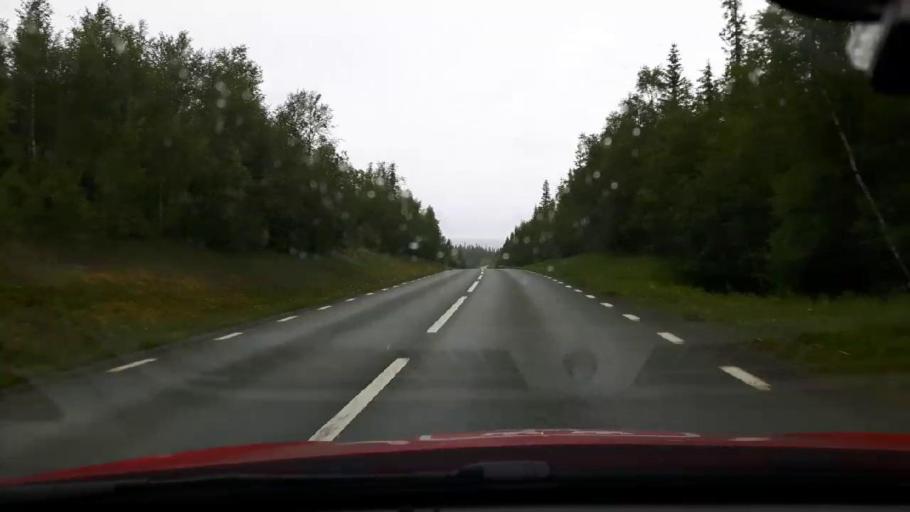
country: NO
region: Nord-Trondelag
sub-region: Meraker
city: Meraker
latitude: 63.2692
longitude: 12.2642
